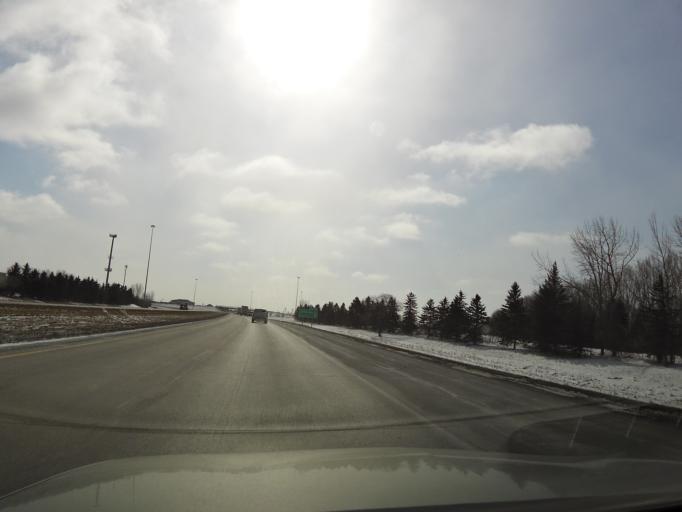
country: US
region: North Dakota
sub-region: Grand Forks County
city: Grand Forks
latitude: 47.8956
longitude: -97.0922
